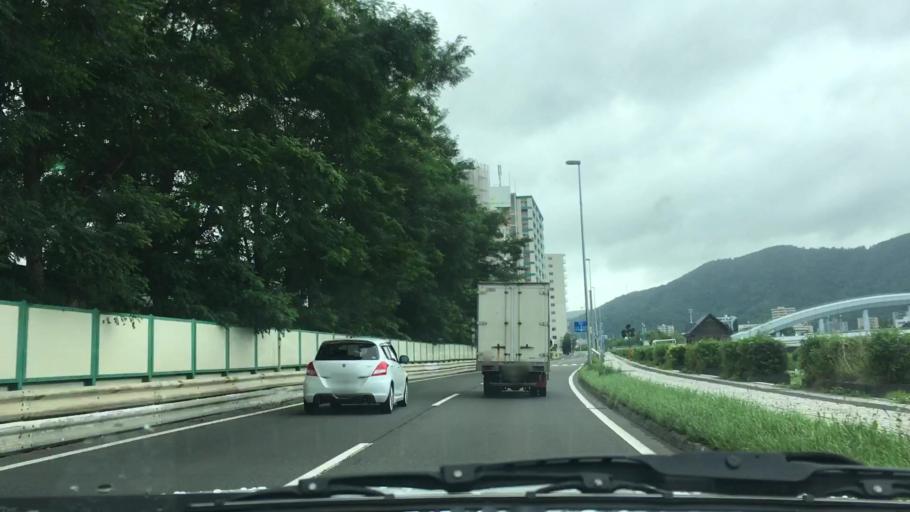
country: JP
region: Hokkaido
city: Sapporo
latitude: 43.0410
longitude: 141.3603
